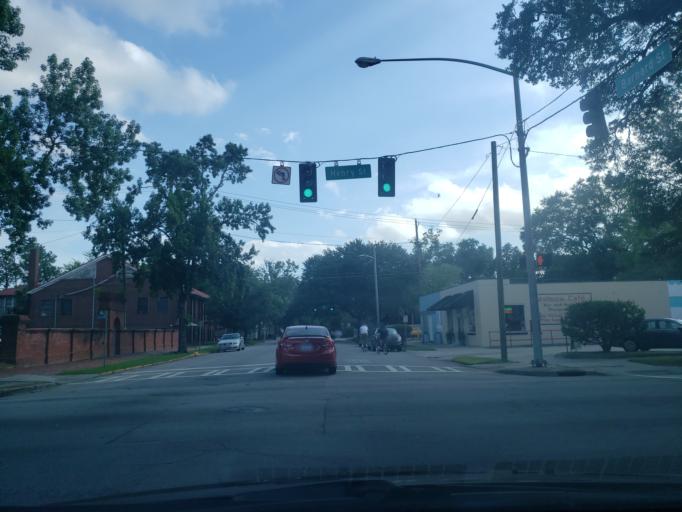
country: US
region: Georgia
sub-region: Chatham County
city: Savannah
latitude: 32.0640
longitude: -81.1001
